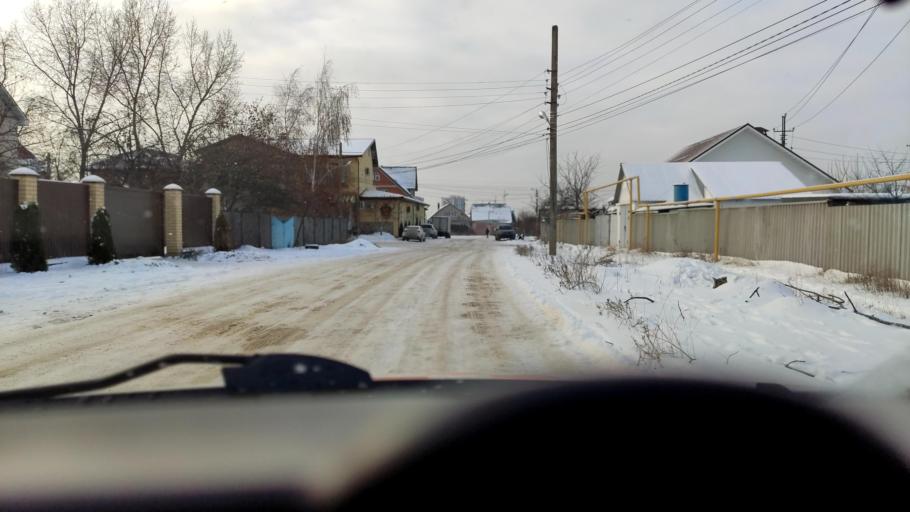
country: RU
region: Voronezj
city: Podgornoye
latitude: 51.7265
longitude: 39.1569
